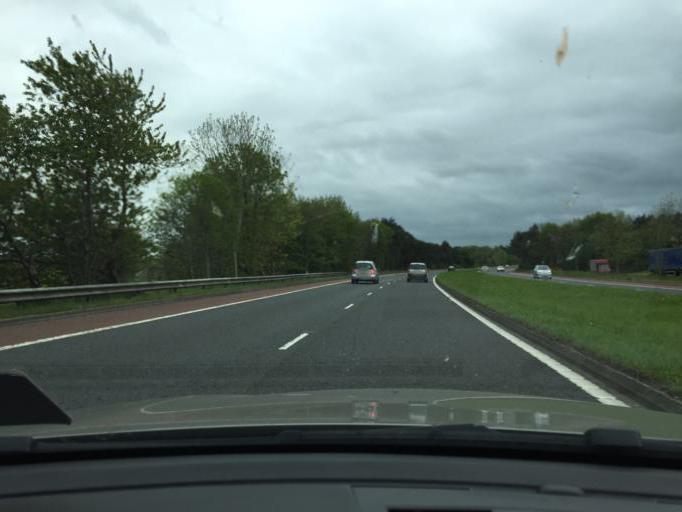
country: GB
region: Northern Ireland
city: Hillsborough
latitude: 54.4482
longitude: -6.1069
